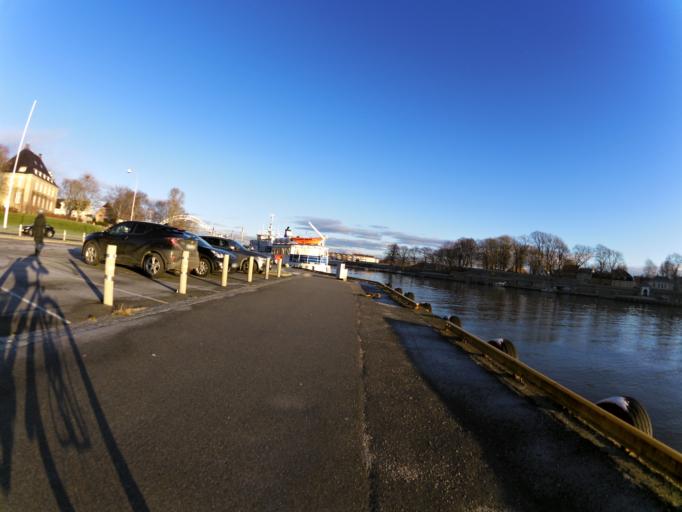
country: NO
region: Ostfold
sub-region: Fredrikstad
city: Fredrikstad
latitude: 59.2052
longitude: 10.9503
